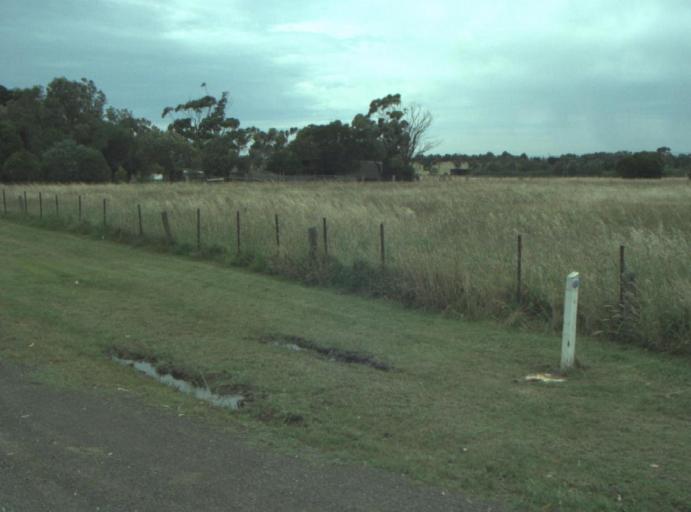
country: AU
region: Victoria
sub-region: Greater Geelong
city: Leopold
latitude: -38.2105
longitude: 144.4507
